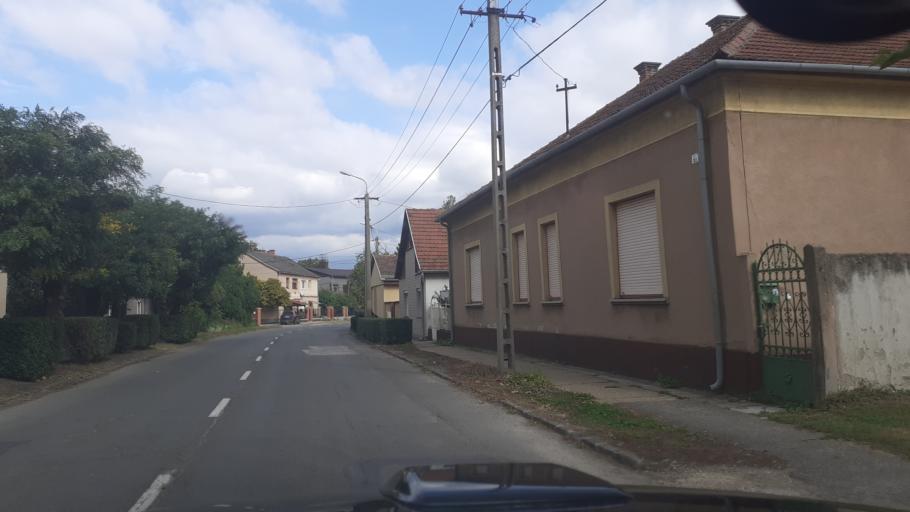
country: HU
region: Bacs-Kiskun
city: Dunavecse
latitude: 46.9190
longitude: 18.9739
